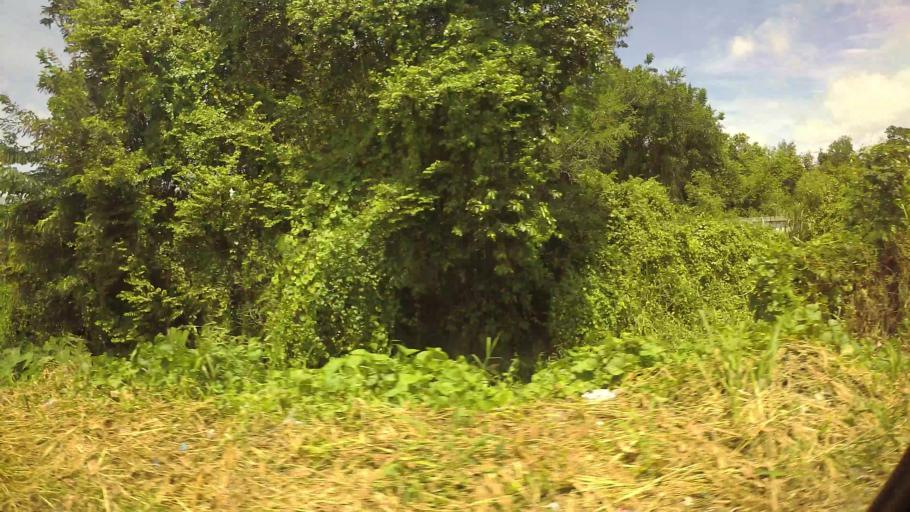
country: TH
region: Chon Buri
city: Sattahip
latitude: 12.7168
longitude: 100.8862
